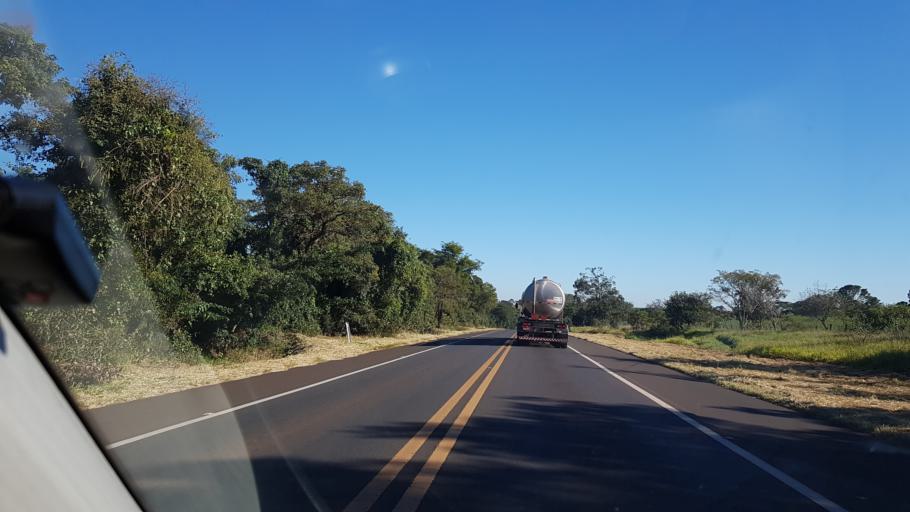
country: BR
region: Sao Paulo
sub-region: Assis
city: Assis
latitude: -22.5833
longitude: -50.5029
